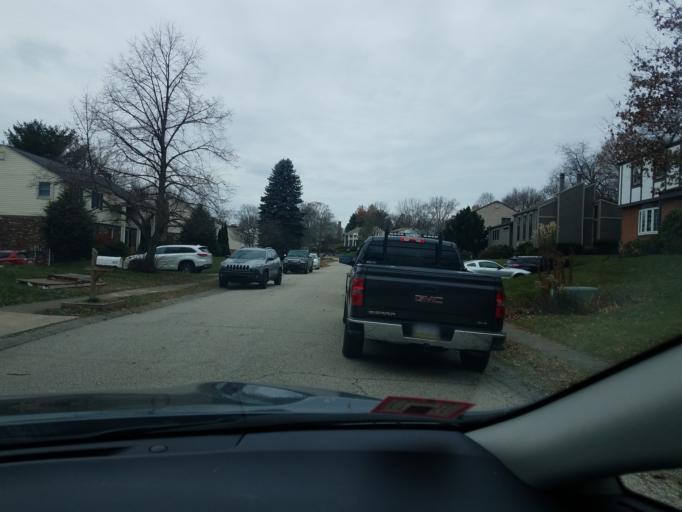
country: US
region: Pennsylvania
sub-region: Allegheny County
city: Franklin Park
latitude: 40.5544
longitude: -80.0607
